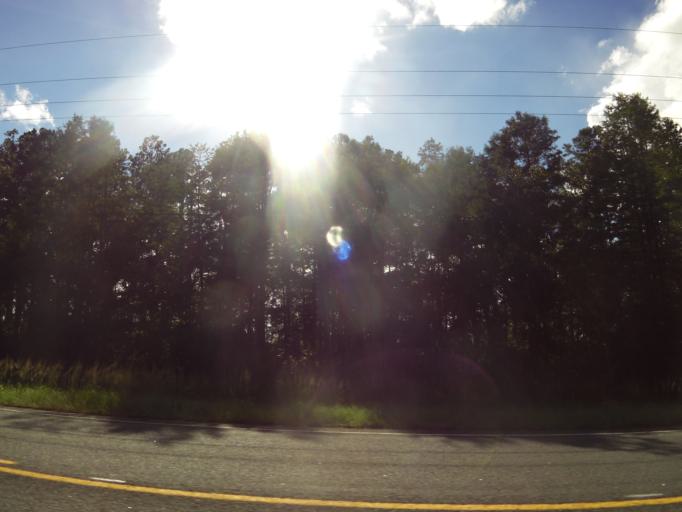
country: US
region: Georgia
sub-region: Camden County
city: Woodbine
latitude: 31.0222
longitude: -81.7310
